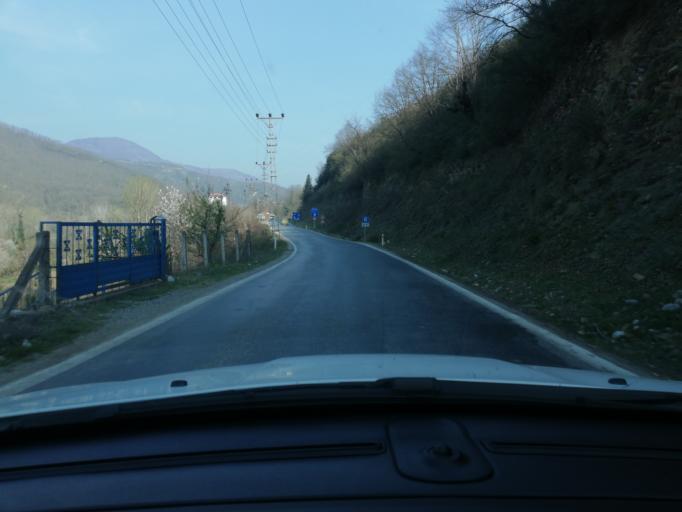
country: TR
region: Karabuk
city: Yenice
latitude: 41.2090
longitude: 32.3669
